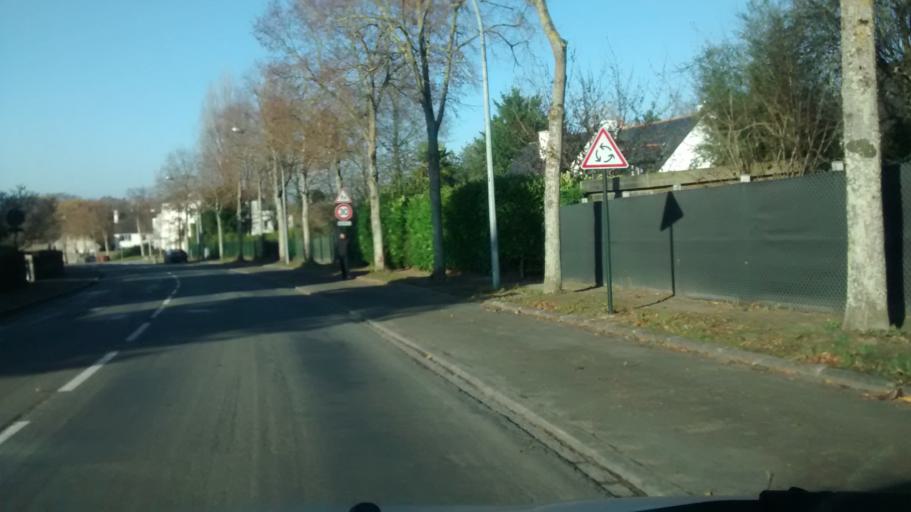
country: FR
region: Brittany
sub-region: Departement d'Ille-et-Vilaine
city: Pace
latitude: 48.1513
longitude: -1.7731
